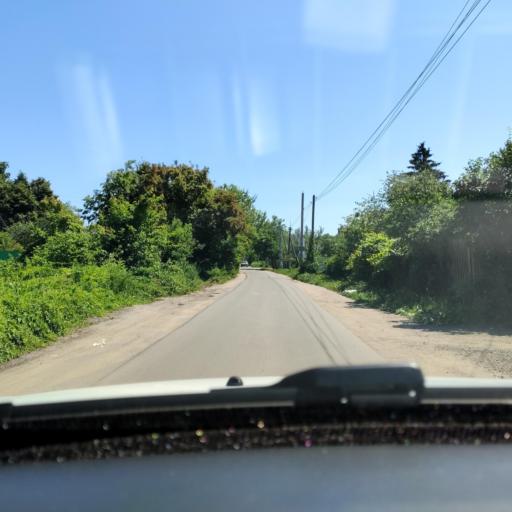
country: RU
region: Voronezj
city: Shilovo
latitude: 51.5844
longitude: 39.1606
